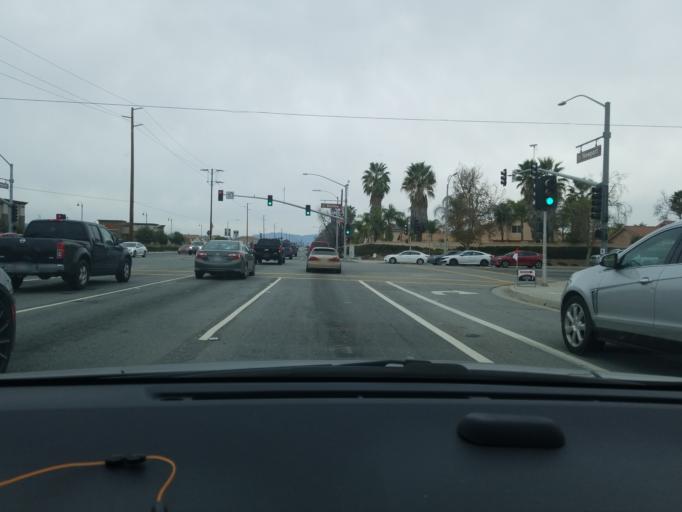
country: US
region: California
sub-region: Riverside County
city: Menifee
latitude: 33.6852
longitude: -117.1534
